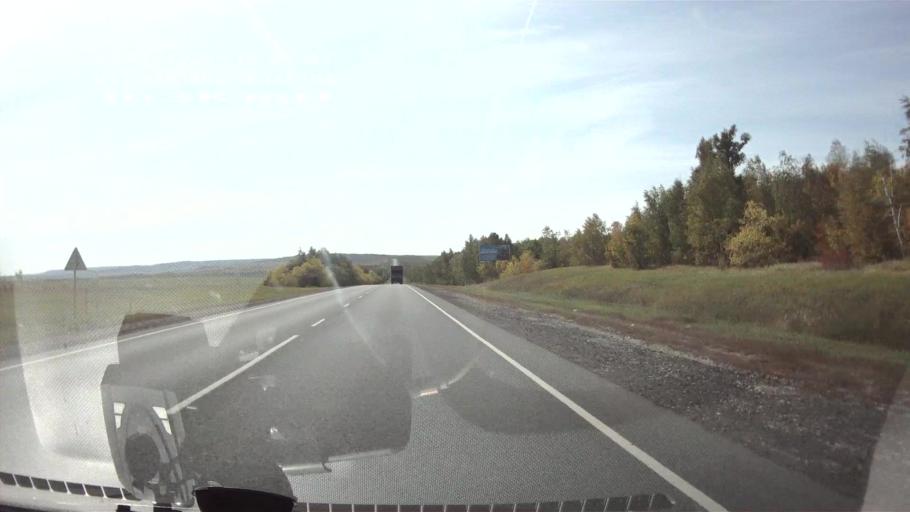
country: RU
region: Saratov
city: Khvalynsk
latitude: 52.5869
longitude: 48.1249
